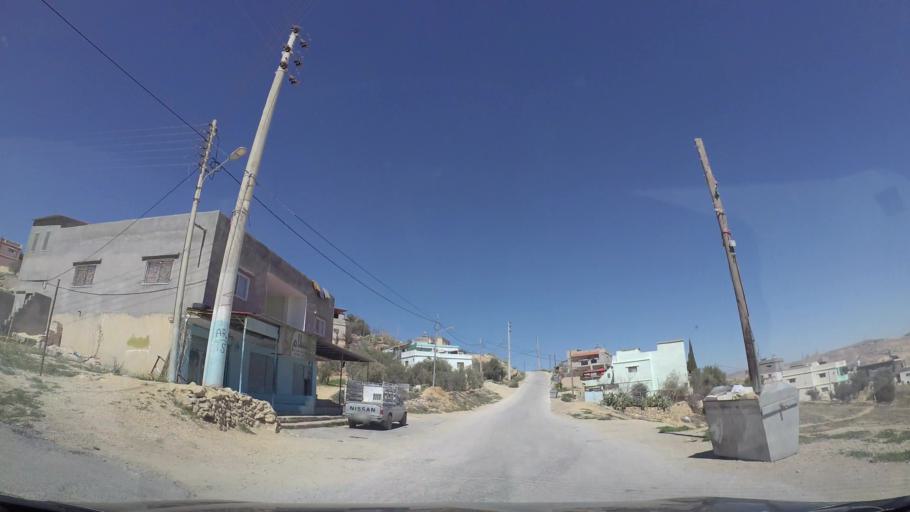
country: JO
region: Tafielah
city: At Tafilah
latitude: 30.8361
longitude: 35.5750
